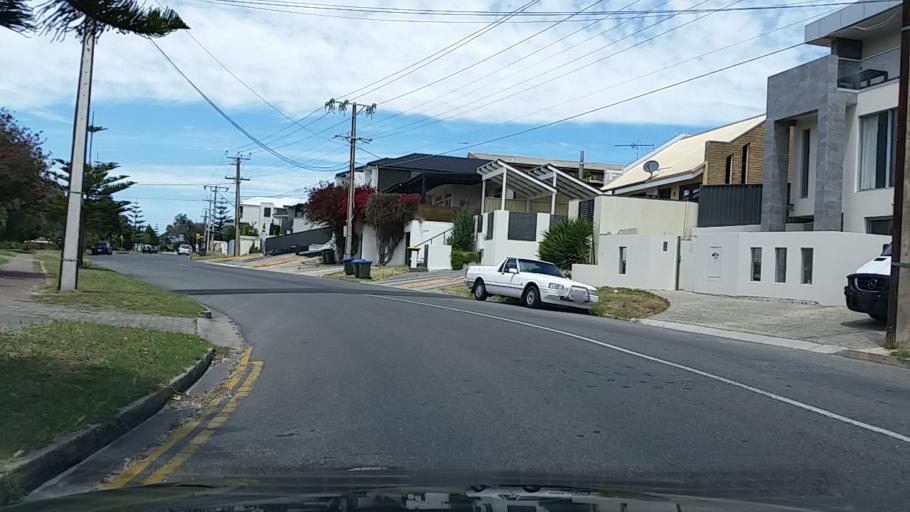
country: AU
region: South Australia
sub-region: Charles Sturt
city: Henley Beach
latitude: -34.9311
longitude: 138.4986
